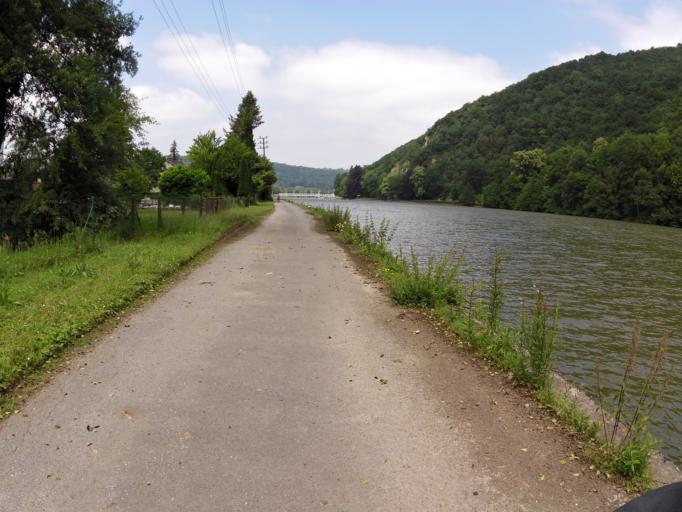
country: BE
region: Wallonia
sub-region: Province de Namur
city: Hastiere-Lavaux
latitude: 50.1940
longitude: 4.8233
